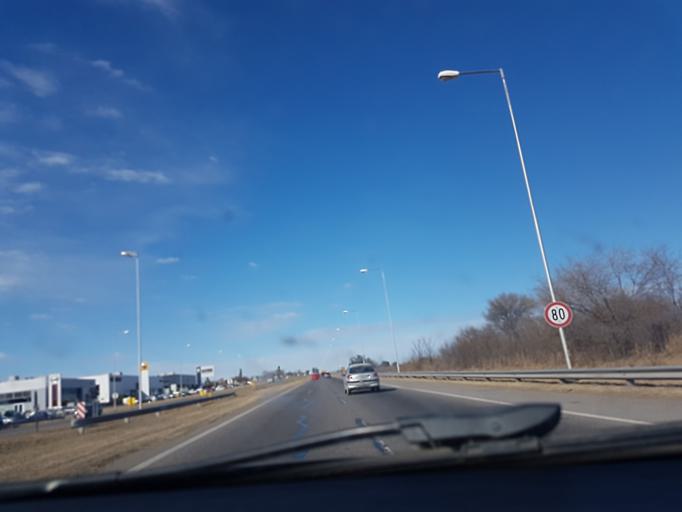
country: AR
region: Cordoba
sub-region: Departamento de Capital
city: Cordoba
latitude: -31.4113
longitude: -64.2696
